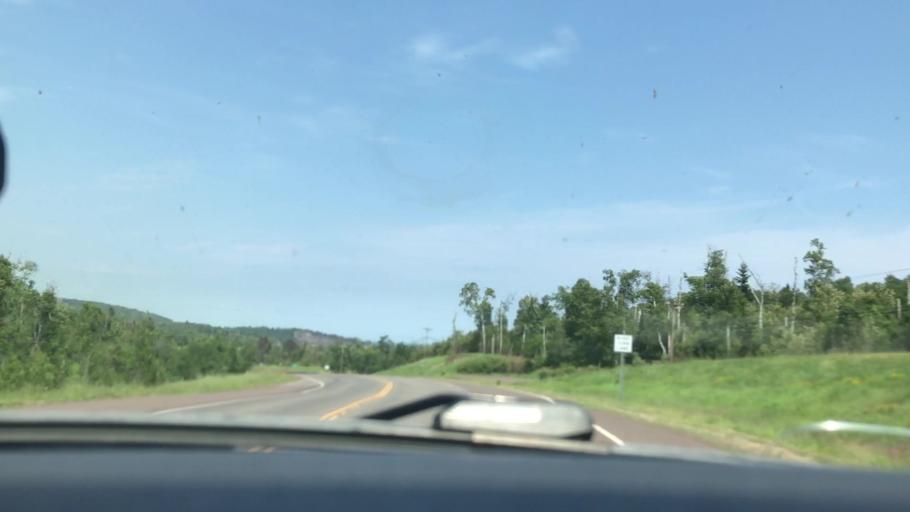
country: US
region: Minnesota
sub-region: Lake County
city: Silver Bay
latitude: 47.3208
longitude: -91.2185
